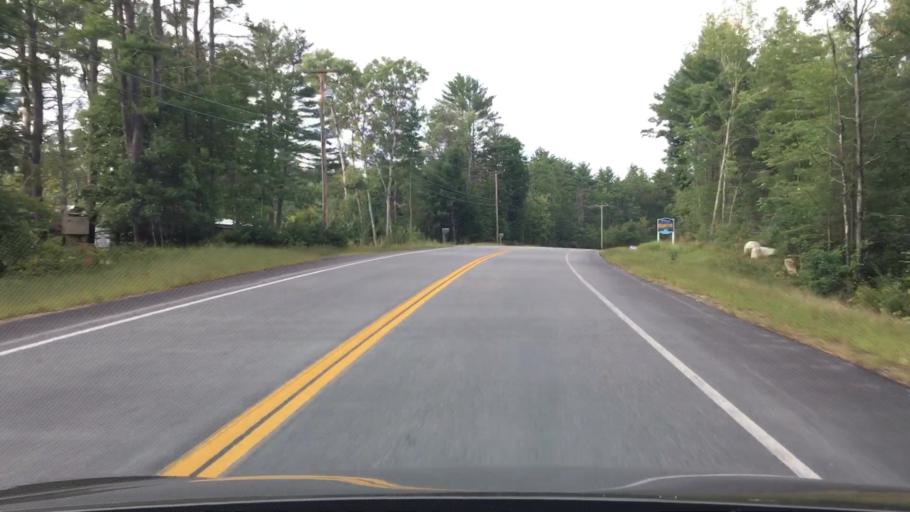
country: US
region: Maine
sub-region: Oxford County
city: Lovell
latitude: 44.0585
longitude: -70.8549
